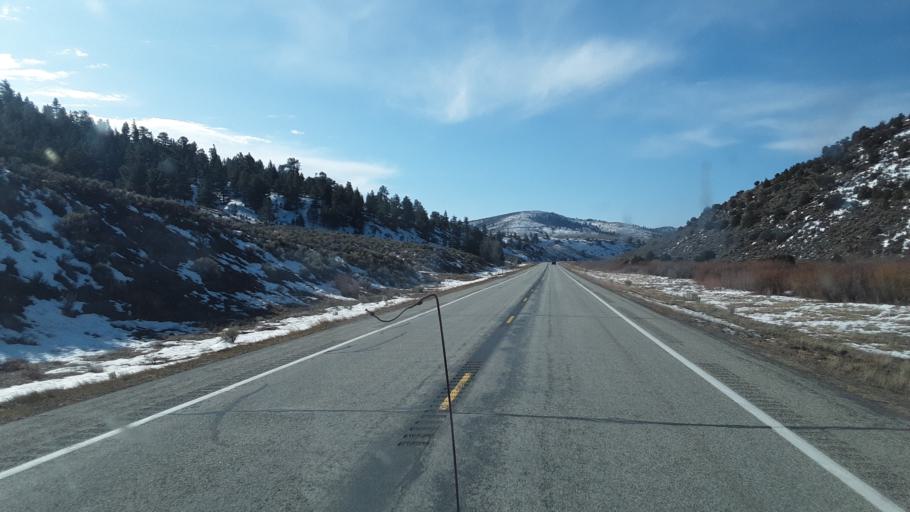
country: US
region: Colorado
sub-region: Costilla County
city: San Luis
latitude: 37.5235
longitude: -105.2987
